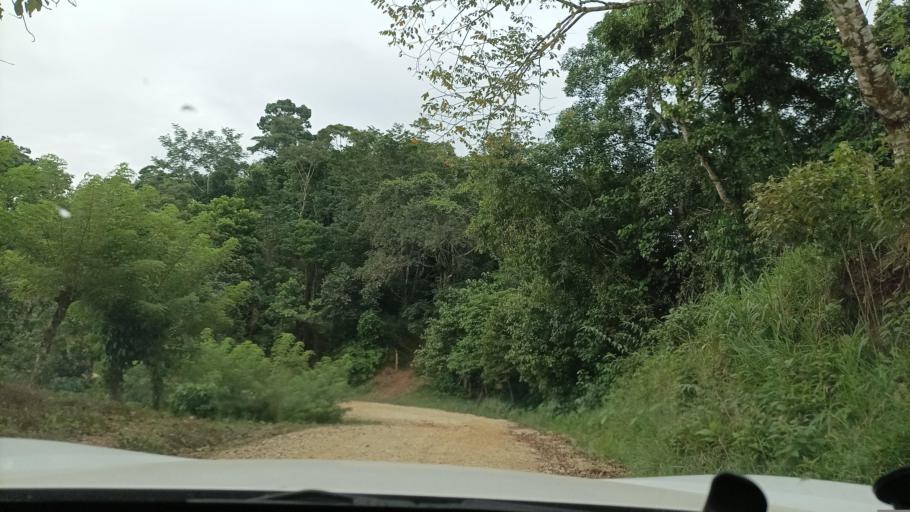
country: MX
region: Veracruz
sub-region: Uxpanapa
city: Poblado 10
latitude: 17.5718
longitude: -94.4225
